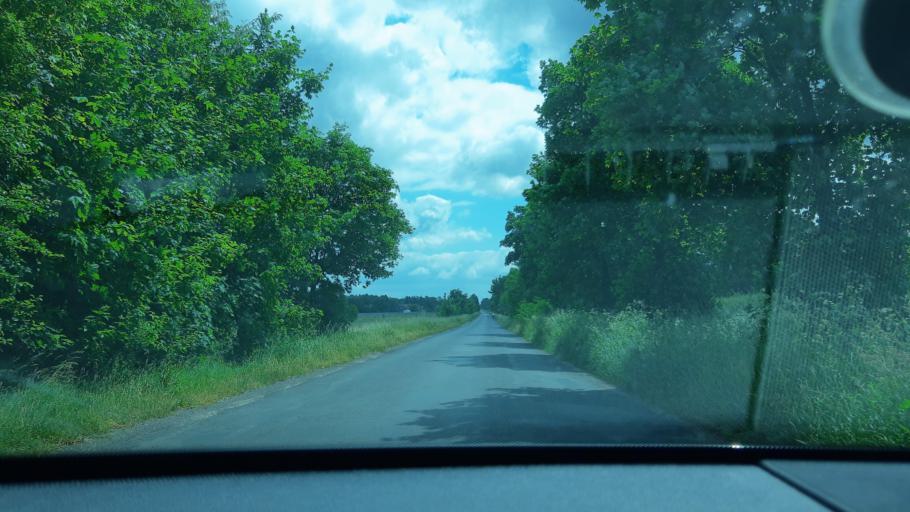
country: PL
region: Lodz Voivodeship
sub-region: Powiat sieradzki
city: Sieradz
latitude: 51.5434
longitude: 18.7899
